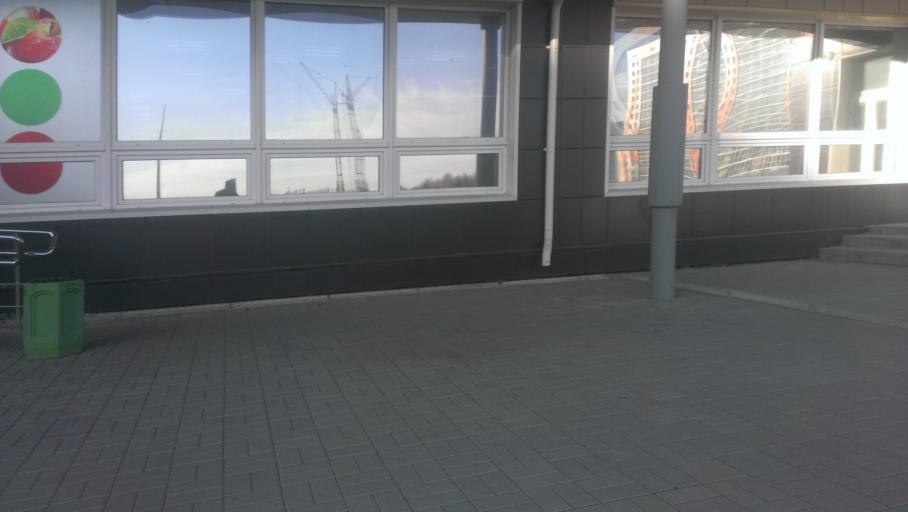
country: RU
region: Altai Krai
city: Novosilikatnyy
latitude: 53.3378
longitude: 83.6543
